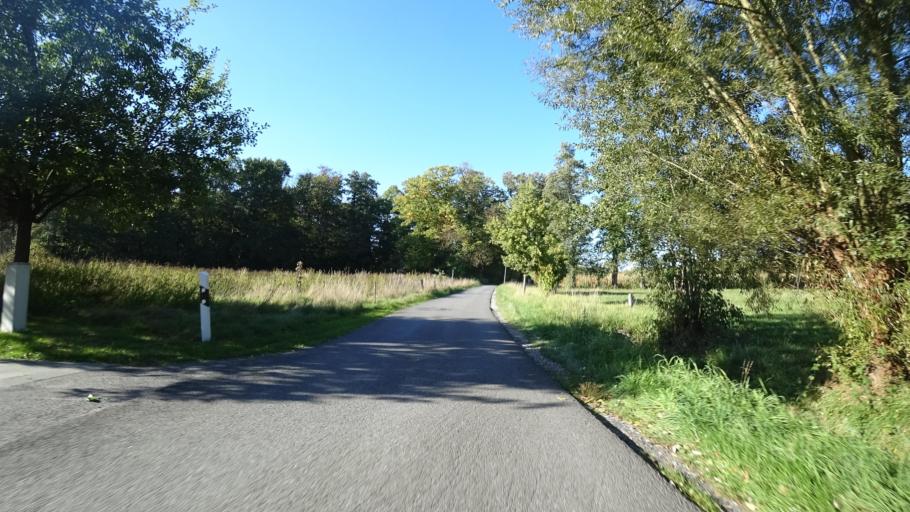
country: DE
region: North Rhine-Westphalia
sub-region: Regierungsbezirk Detmold
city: Guetersloh
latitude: 51.8760
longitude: 8.3600
